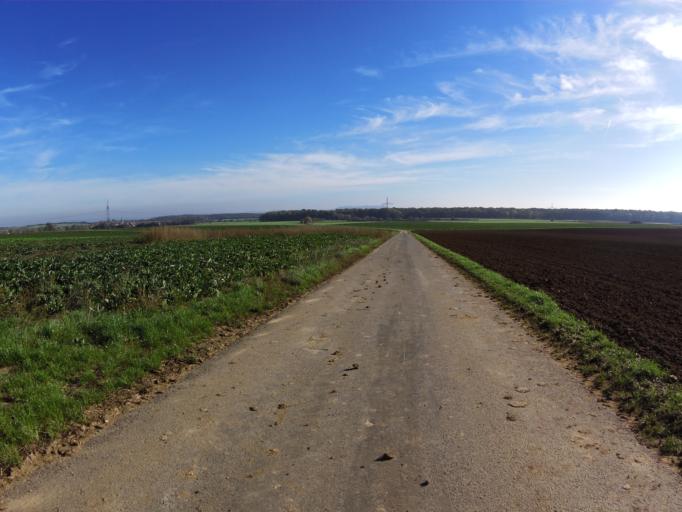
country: DE
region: Bavaria
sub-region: Regierungsbezirk Unterfranken
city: Theilheim
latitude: 49.7219
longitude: 10.0700
